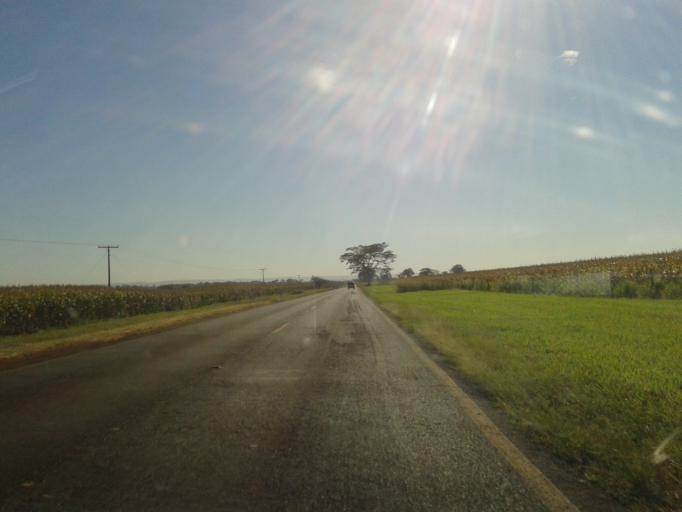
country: BR
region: Minas Gerais
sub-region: Capinopolis
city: Capinopolis
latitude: -18.6156
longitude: -49.5307
